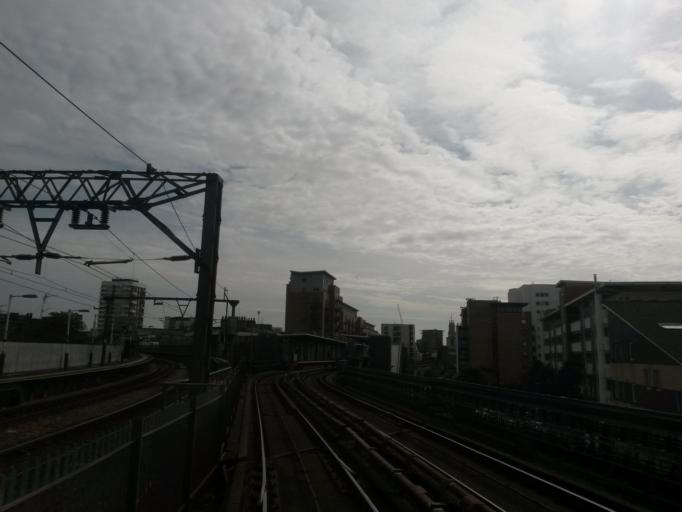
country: GB
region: England
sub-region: Greater London
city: Bethnal Green
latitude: 51.5123
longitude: -0.0409
